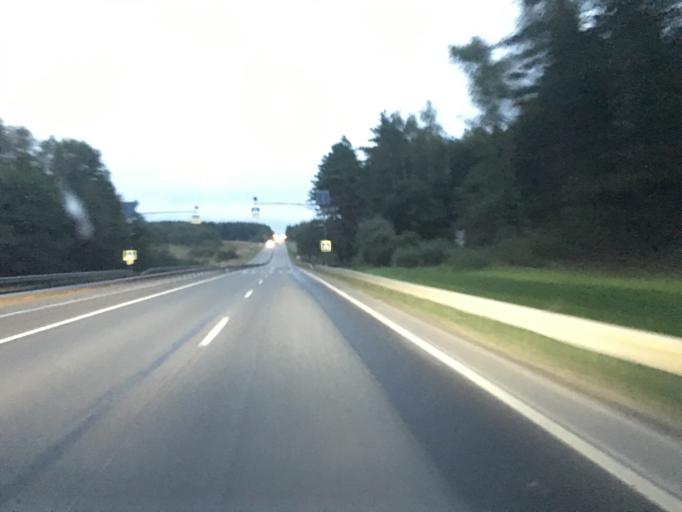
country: RU
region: Kaluga
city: Maloyaroslavets
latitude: 54.9638
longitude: 36.4681
